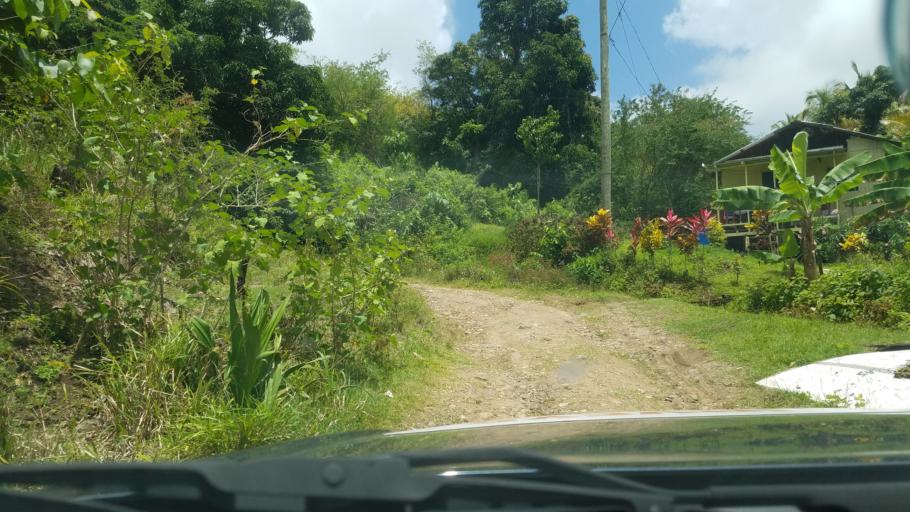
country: LC
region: Gros-Islet
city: Gros Islet
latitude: 14.0518
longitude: -60.9278
